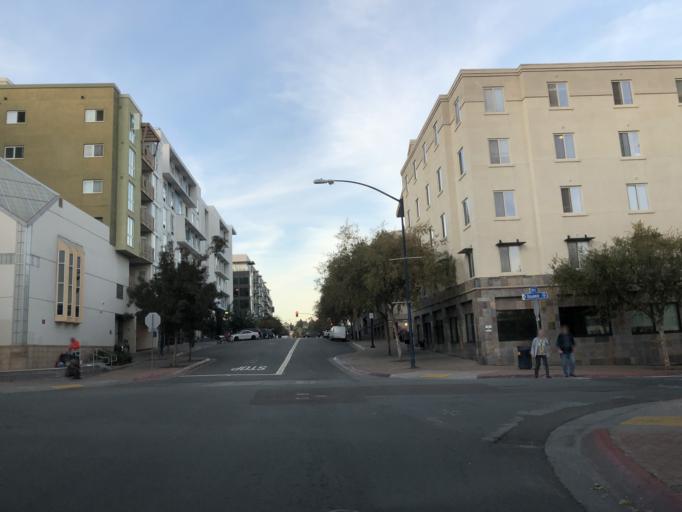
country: US
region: California
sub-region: San Diego County
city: San Diego
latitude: 32.7103
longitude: -117.1519
